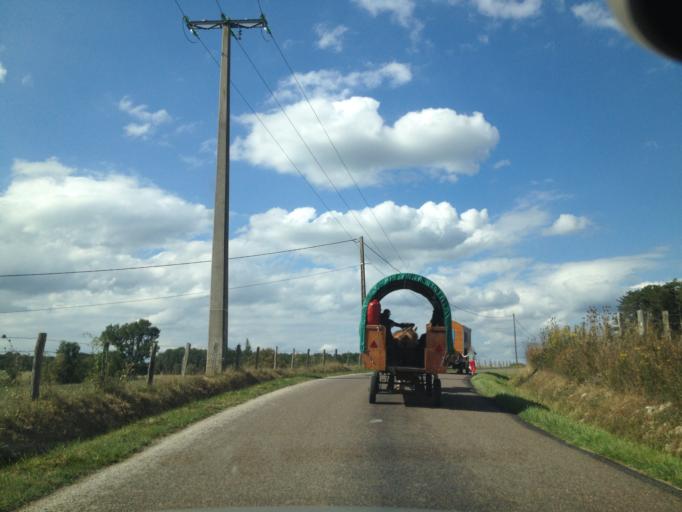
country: FR
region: Franche-Comte
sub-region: Departement de la Haute-Saone
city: Saint-Loup-sur-Semouse
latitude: 47.8252
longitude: 6.2072
